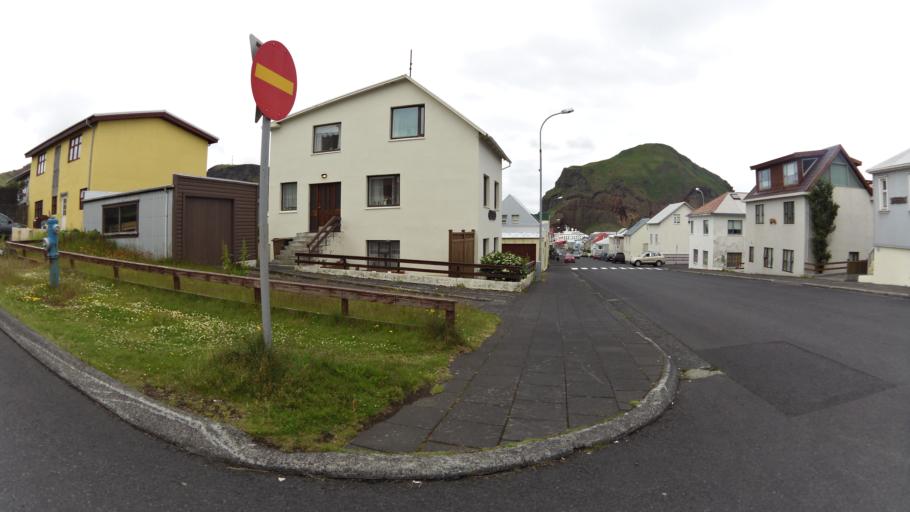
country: IS
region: South
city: Vestmannaeyjar
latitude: 63.4380
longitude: -20.2714
